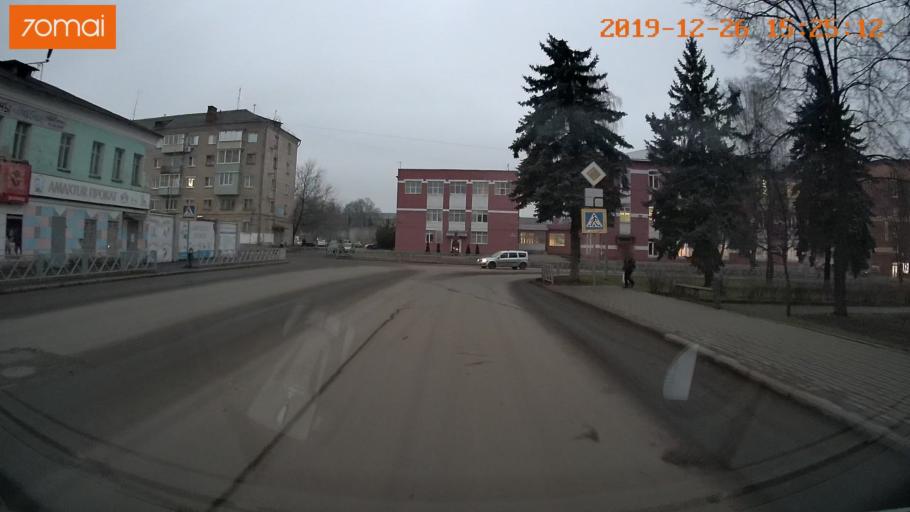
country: RU
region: Jaroslavl
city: Rybinsk
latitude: 58.0526
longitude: 38.8393
